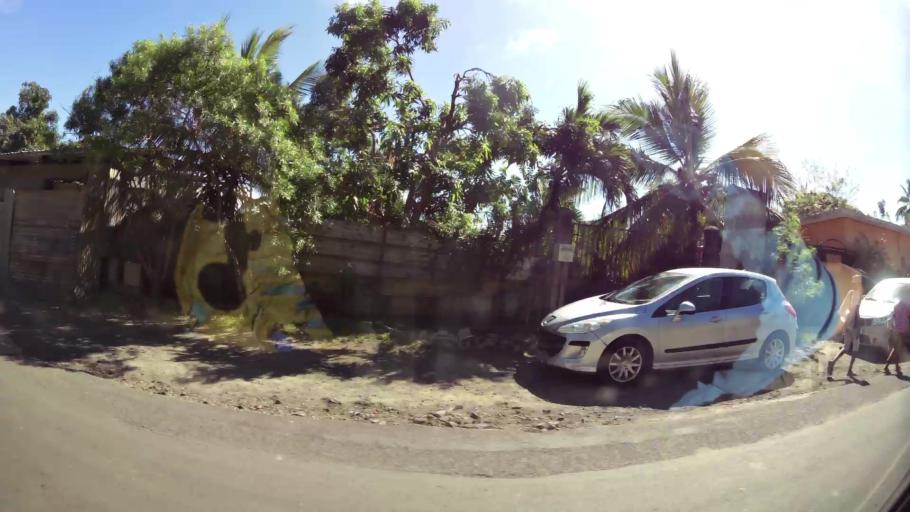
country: YT
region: Pamandzi
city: Pamandzi
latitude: -12.7783
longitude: 45.2815
